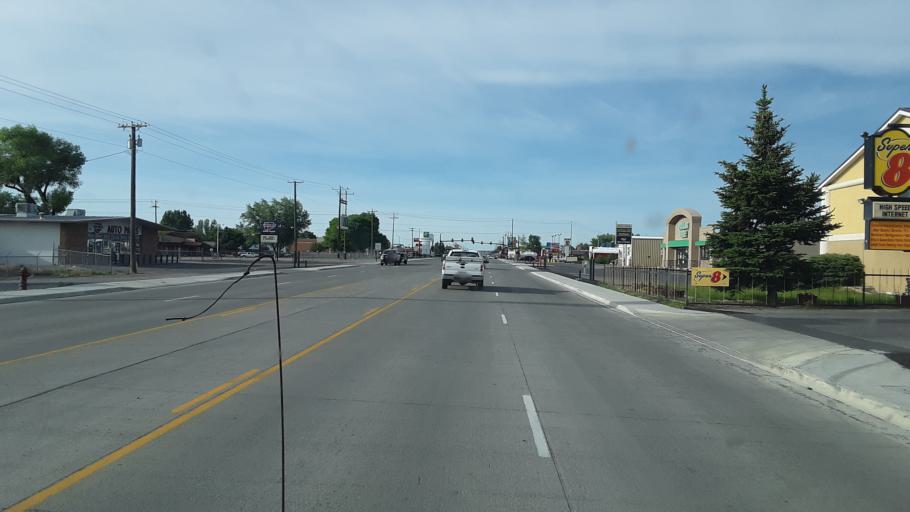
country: US
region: Wyoming
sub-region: Fremont County
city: Riverton
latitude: 43.0367
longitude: -108.3807
